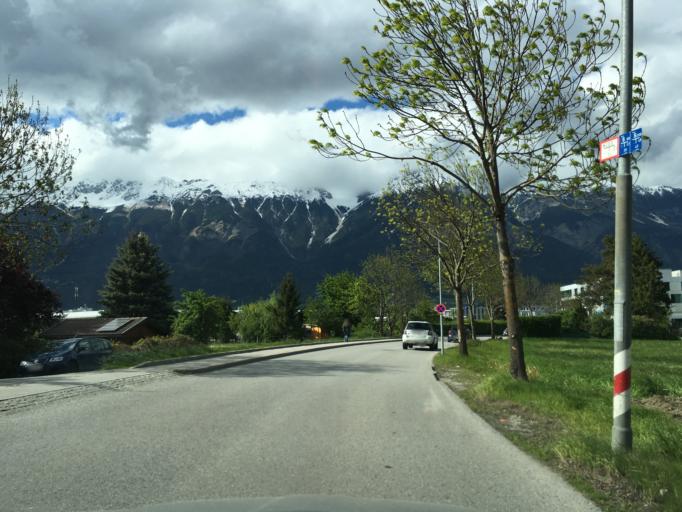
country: AT
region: Tyrol
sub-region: Politischer Bezirk Innsbruck Land
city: Ampass
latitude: 47.2605
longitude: 11.4343
